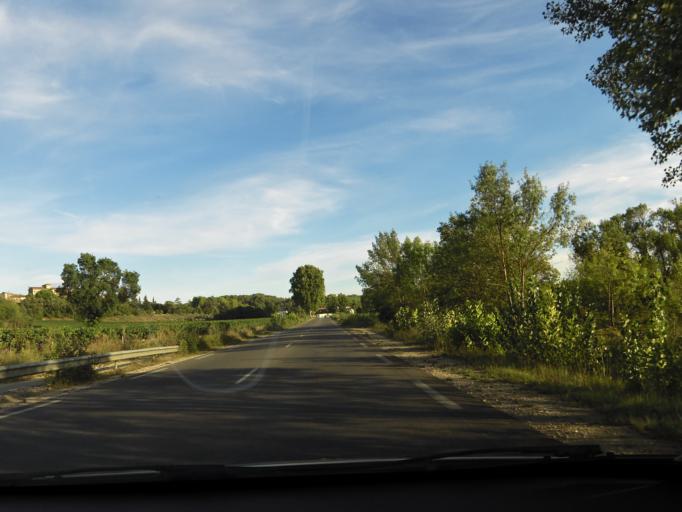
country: FR
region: Languedoc-Roussillon
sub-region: Departement de l'Herault
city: Prades-le-Lez
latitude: 43.6808
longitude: 3.8654
